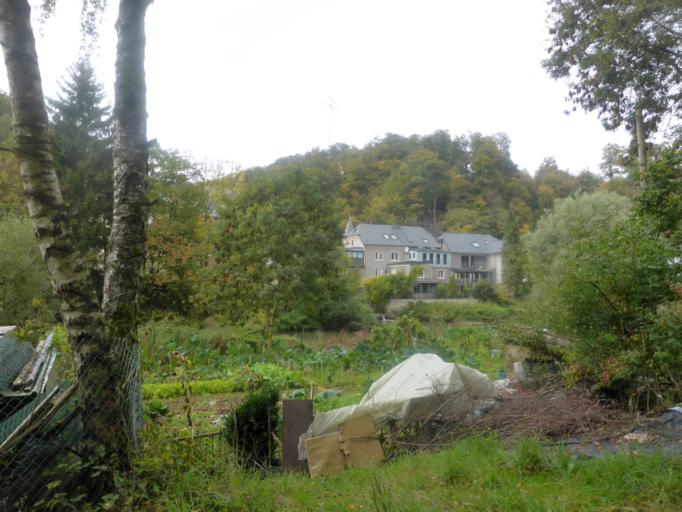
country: LU
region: Luxembourg
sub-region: Canton de Luxembourg
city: Hesperange
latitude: 49.5743
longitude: 6.1549
